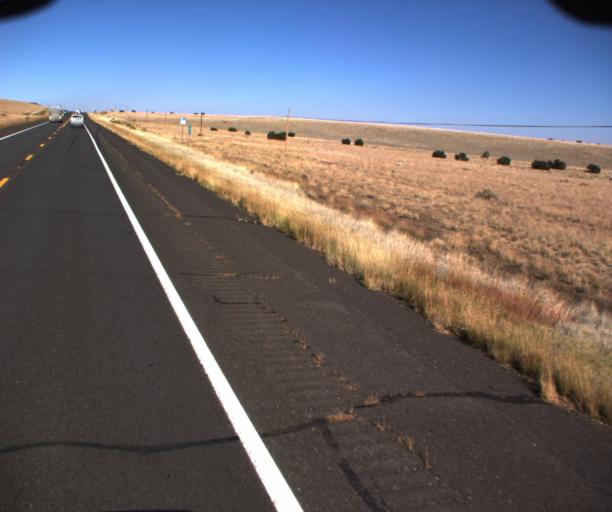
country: US
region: Arizona
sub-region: Coconino County
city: Flagstaff
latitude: 35.5629
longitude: -111.5337
